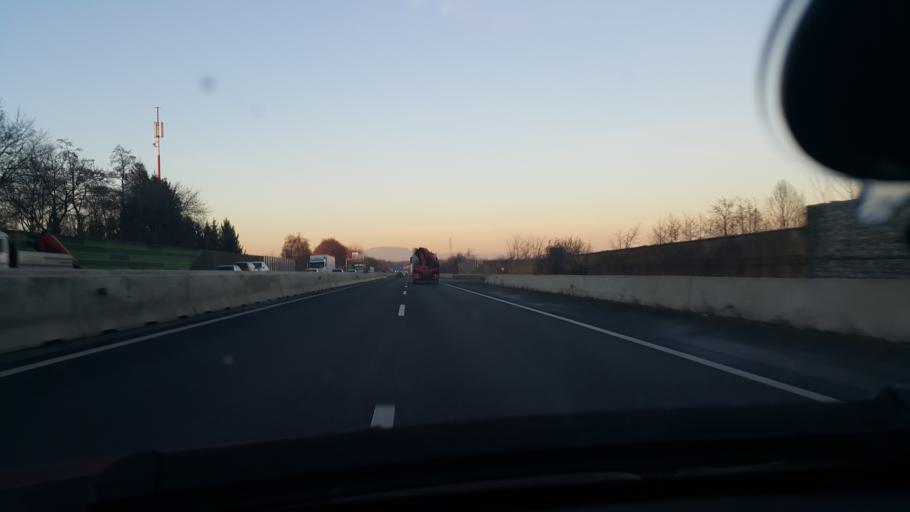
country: AT
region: Styria
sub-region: Politischer Bezirk Leibnitz
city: Weitendorf
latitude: 46.8954
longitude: 15.4721
